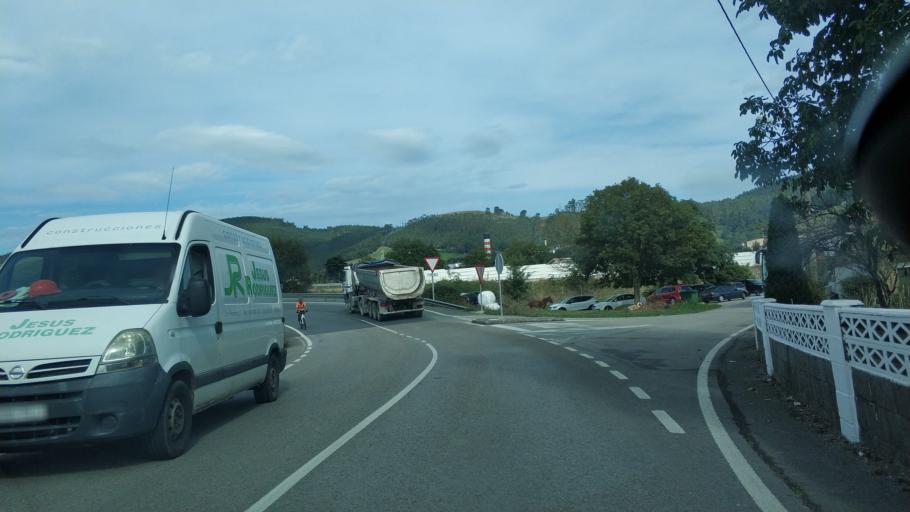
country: ES
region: Cantabria
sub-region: Provincia de Cantabria
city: Santa Maria de Cayon
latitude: 43.3113
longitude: -3.8787
